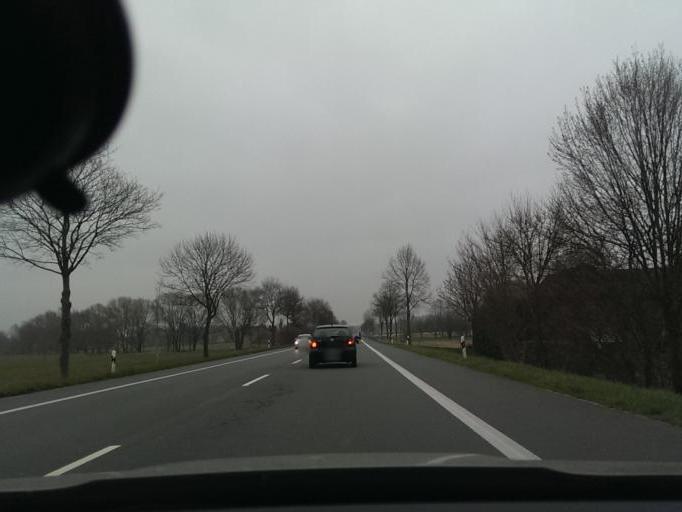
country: DE
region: North Rhine-Westphalia
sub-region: Regierungsbezirk Detmold
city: Delbruck
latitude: 51.7780
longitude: 8.5067
